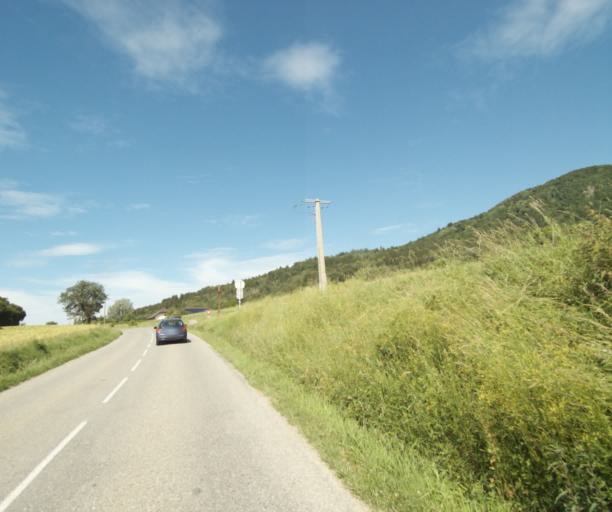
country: FR
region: Rhone-Alpes
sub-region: Departement de la Haute-Savoie
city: Perrignier
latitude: 46.2988
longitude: 6.4552
